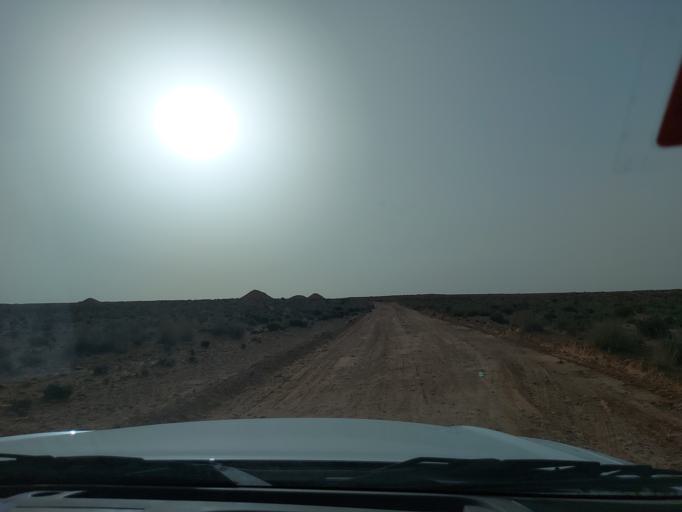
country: TN
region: Madanin
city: Medenine
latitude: 33.2856
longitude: 10.5967
